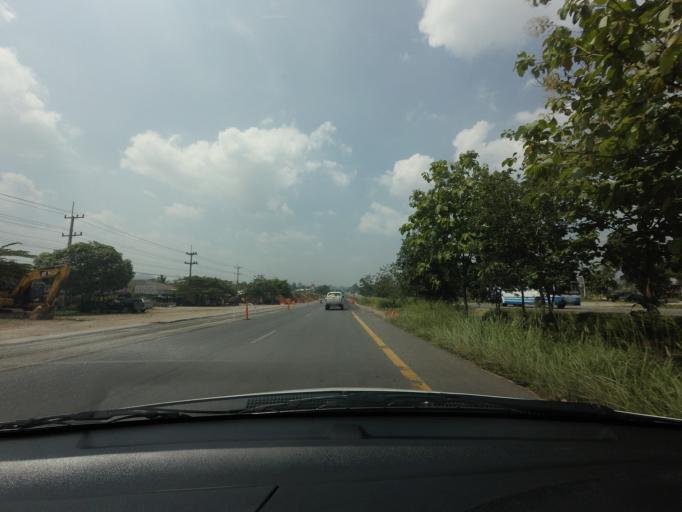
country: TH
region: Nakhon Ratchasima
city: Pak Chong
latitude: 14.6640
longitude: 101.4158
